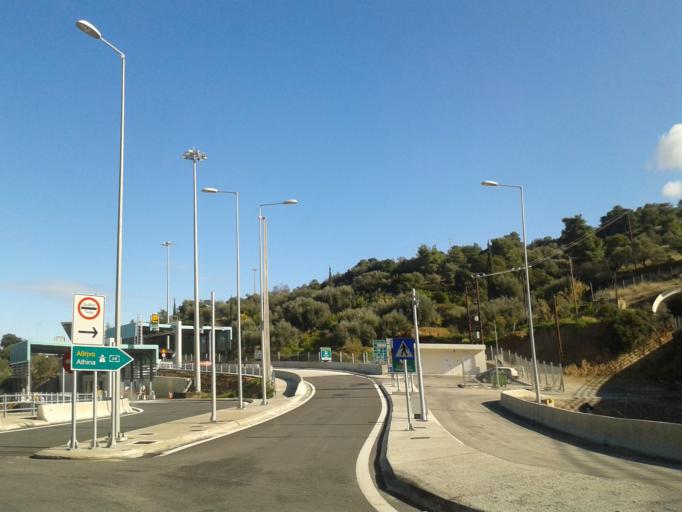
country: GR
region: West Greece
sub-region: Nomos Achaias
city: Akrata
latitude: 38.1743
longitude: 22.2383
